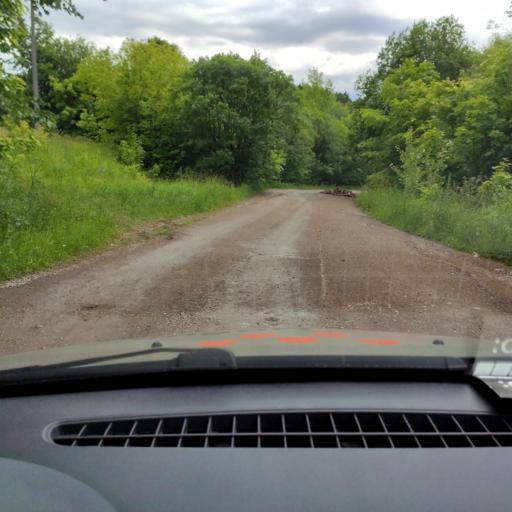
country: RU
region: Bashkortostan
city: Iglino
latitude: 54.8919
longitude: 56.2797
